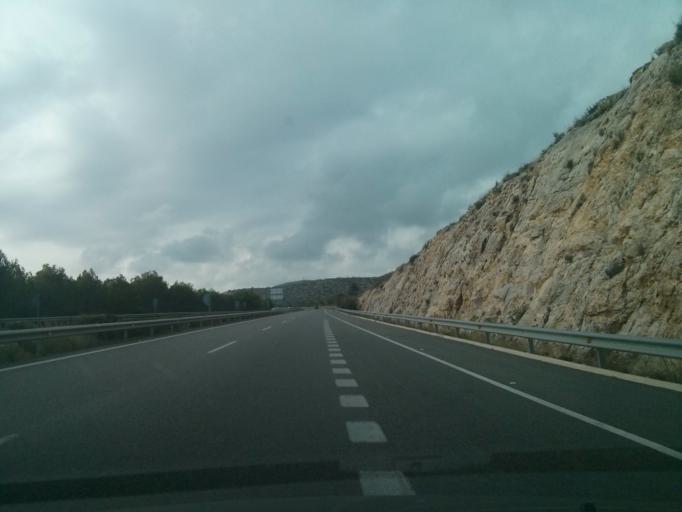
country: ES
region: Catalonia
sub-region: Provincia de Barcelona
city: Vilanova i la Geltru
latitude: 41.2497
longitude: 1.7061
